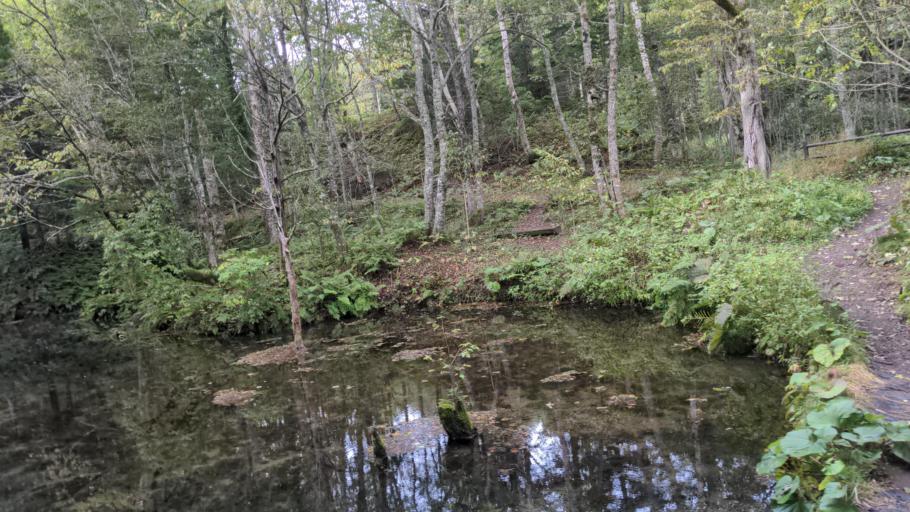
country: JP
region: Hokkaido
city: Abashiri
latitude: 43.6455
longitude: 144.5498
